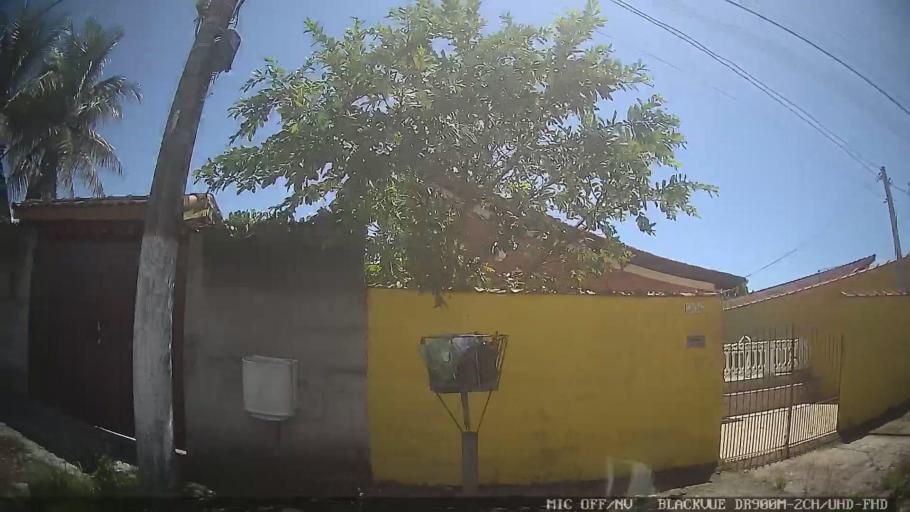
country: BR
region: Sao Paulo
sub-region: Caraguatatuba
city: Caraguatatuba
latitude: -23.6903
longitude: -45.4360
